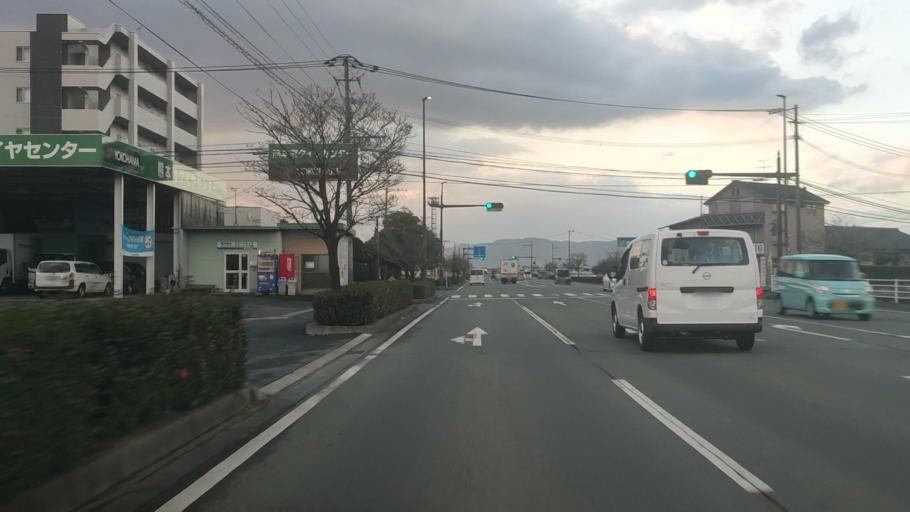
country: JP
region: Kumamoto
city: Kumamoto
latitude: 32.7597
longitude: 130.7058
